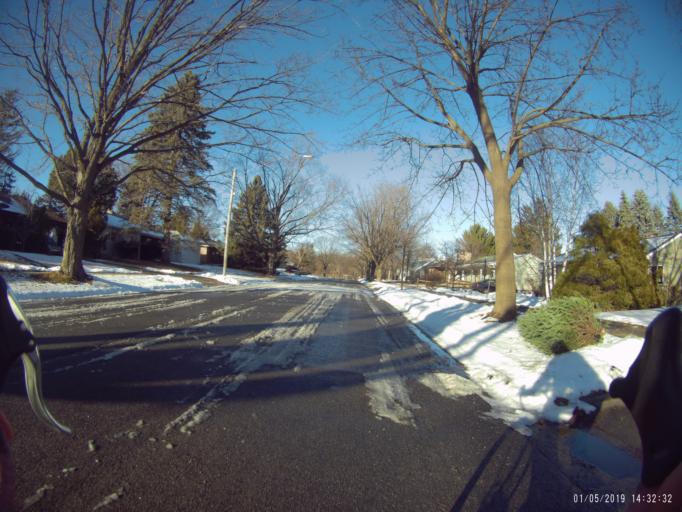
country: US
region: Wisconsin
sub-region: Dane County
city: Shorewood Hills
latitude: 43.0519
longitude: -89.4456
